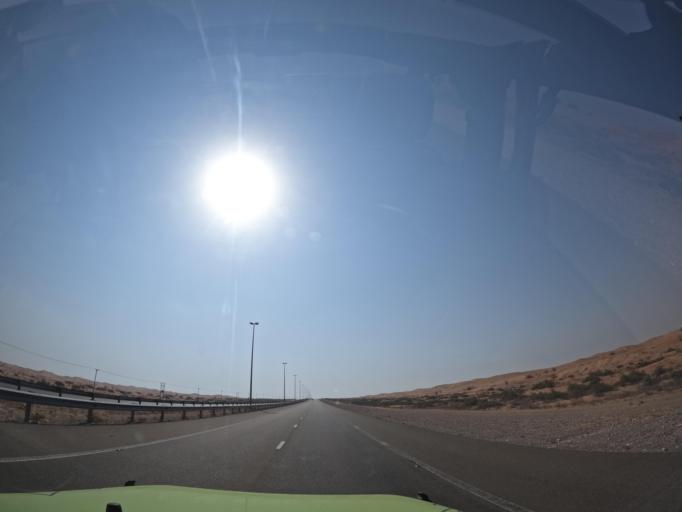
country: OM
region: Al Buraimi
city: Al Buraymi
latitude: 24.4517
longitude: 55.6509
